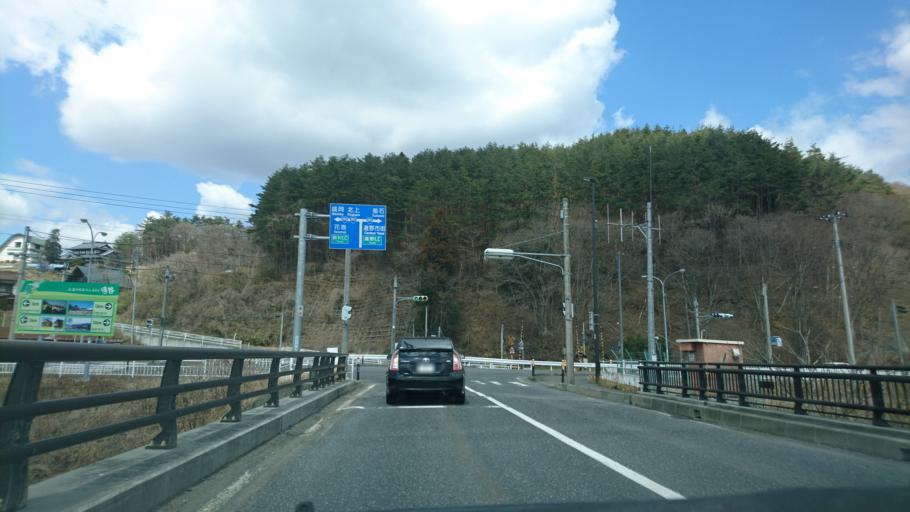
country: JP
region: Iwate
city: Tono
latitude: 39.2999
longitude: 141.4021
